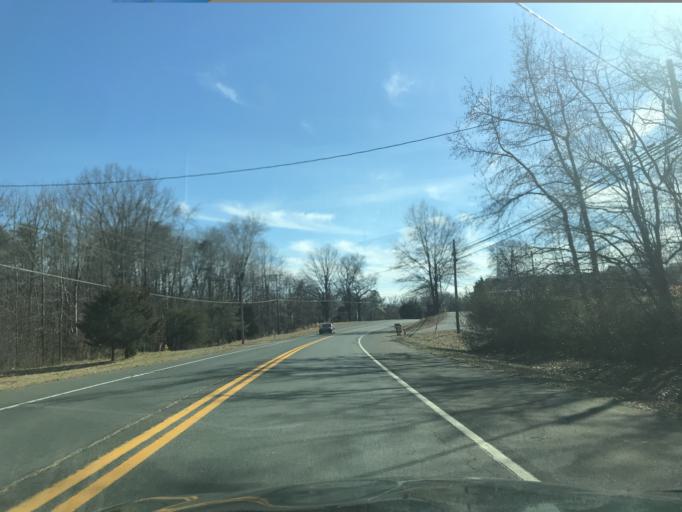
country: US
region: Maryland
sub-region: Charles County
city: Bryans Road
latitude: 38.6406
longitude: -77.0709
